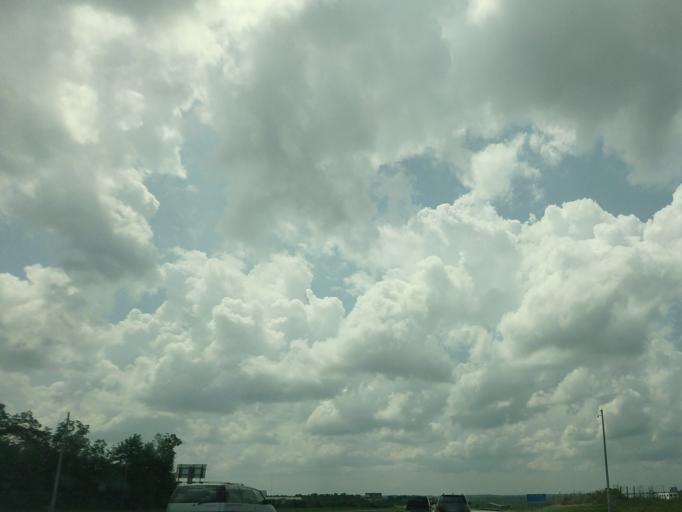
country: US
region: Georgia
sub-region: Peach County
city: Byron
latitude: 32.7338
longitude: -83.7239
